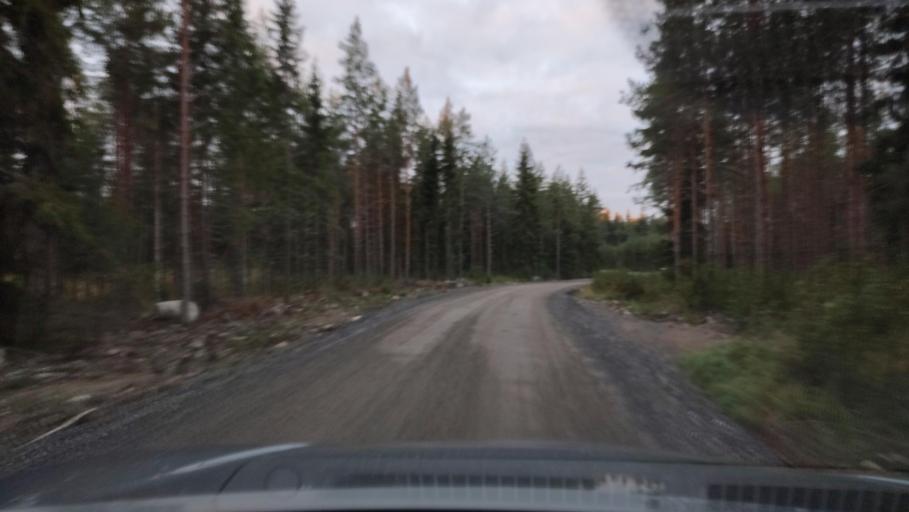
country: FI
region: Southern Ostrobothnia
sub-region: Suupohja
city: Karijoki
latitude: 62.1873
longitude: 21.5889
